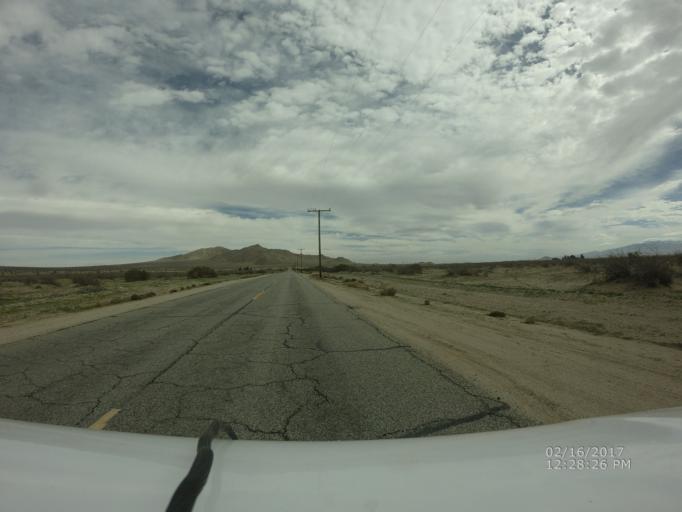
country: US
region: California
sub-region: Los Angeles County
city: Lake Los Angeles
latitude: 34.6679
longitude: -117.8397
